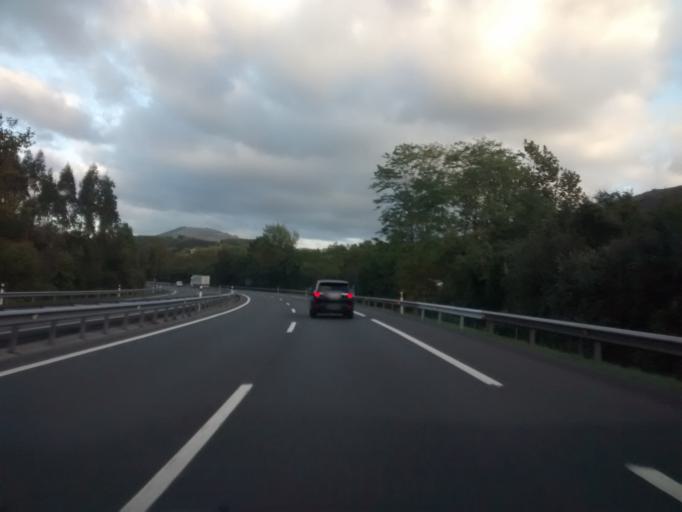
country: ES
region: Basque Country
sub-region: Provincia de Guipuzcoa
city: Cestona
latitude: 43.2594
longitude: -2.2875
